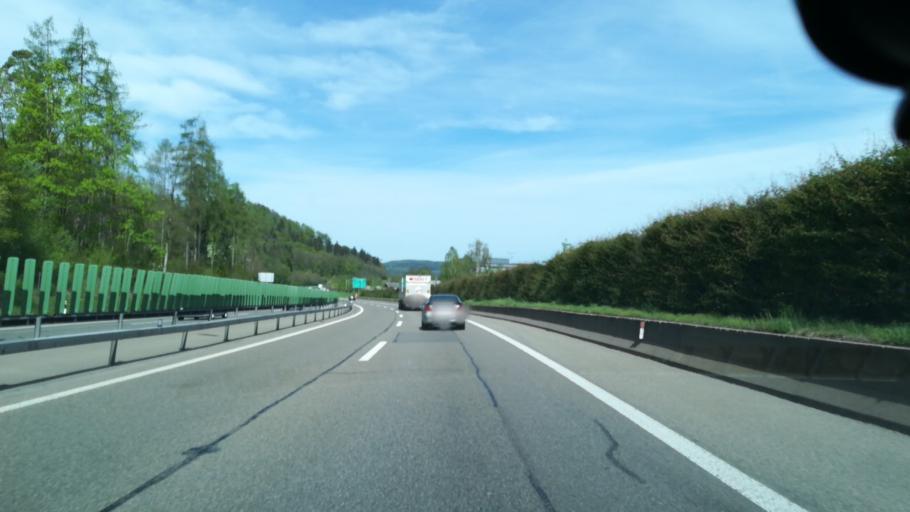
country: CH
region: Zurich
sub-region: Bezirk Winterthur
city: Toess (Kreis 4) / Schlosstal
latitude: 47.4931
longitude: 8.7007
